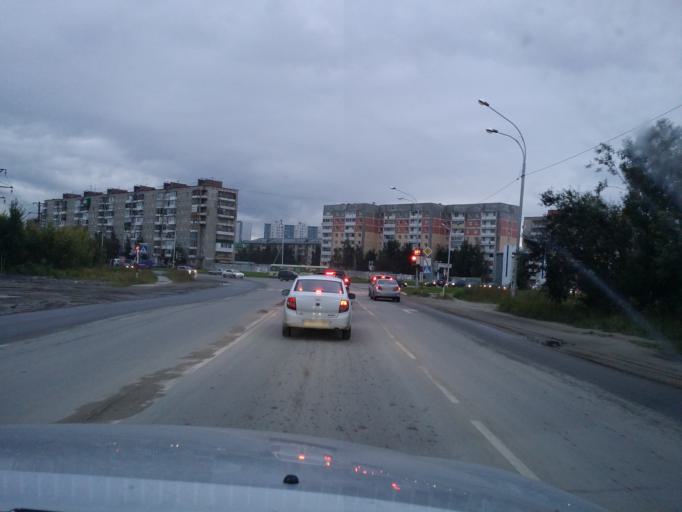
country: RU
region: Khanty-Mansiyskiy Avtonomnyy Okrug
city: Nizhnevartovsk
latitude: 60.9408
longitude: 76.6207
